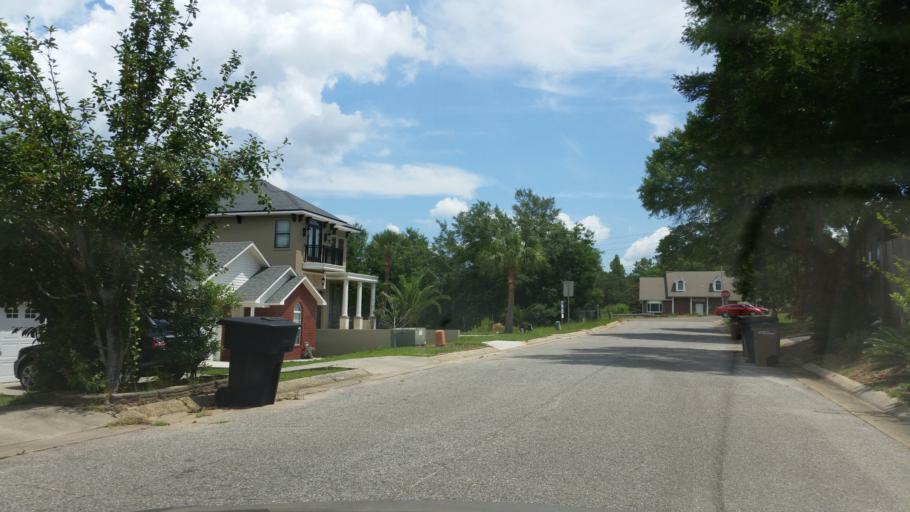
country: US
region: Florida
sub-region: Escambia County
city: Brent
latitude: 30.4801
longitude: -87.2203
